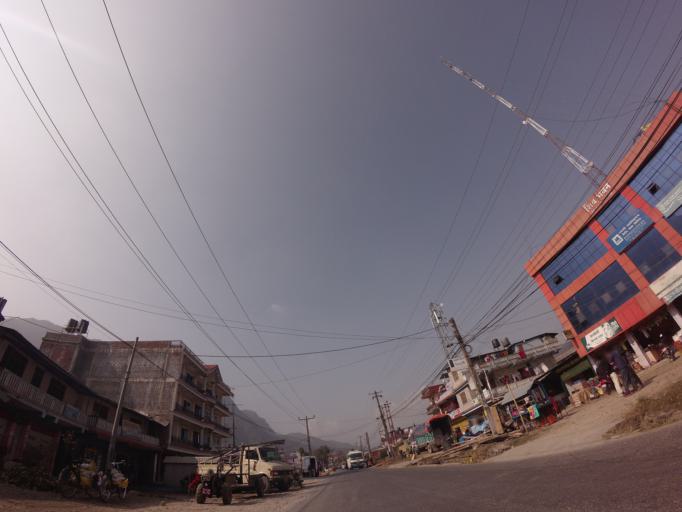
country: NP
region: Western Region
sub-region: Gandaki Zone
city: Pokhara
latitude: 28.2778
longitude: 83.9357
